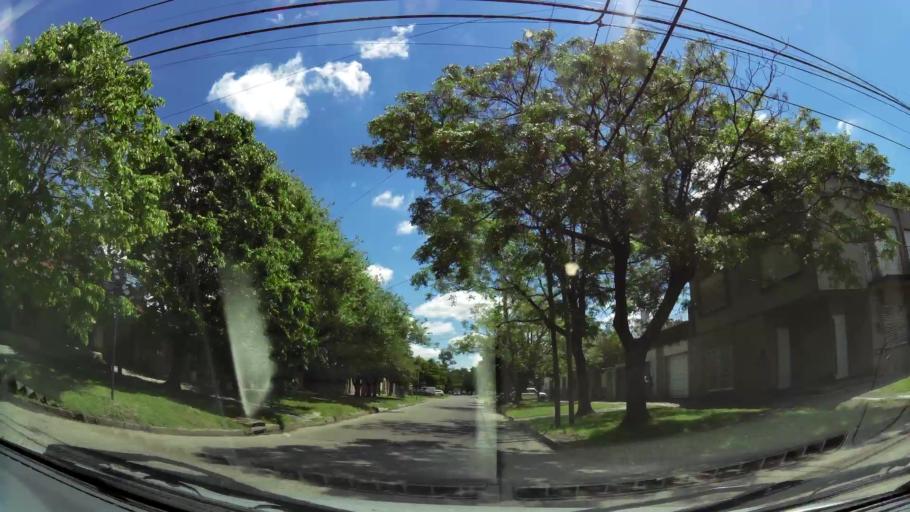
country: AR
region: Buenos Aires
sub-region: Partido de Lomas de Zamora
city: Lomas de Zamora
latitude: -34.7370
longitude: -58.4193
